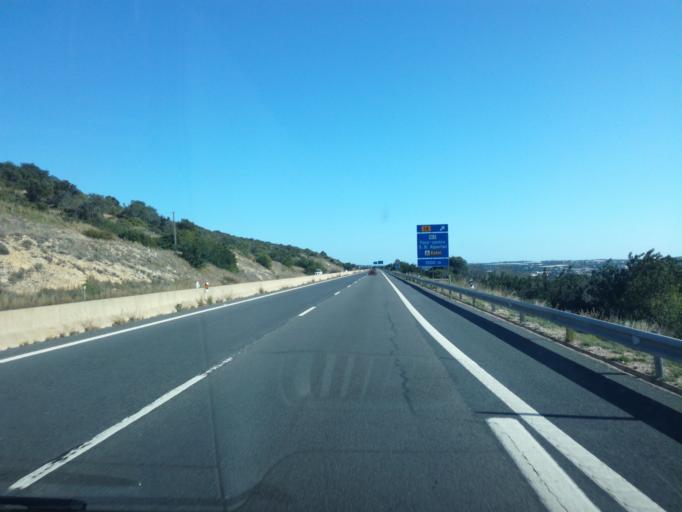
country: PT
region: Faro
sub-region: Faro
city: Santa Barbara de Nexe
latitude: 37.0944
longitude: -7.9348
